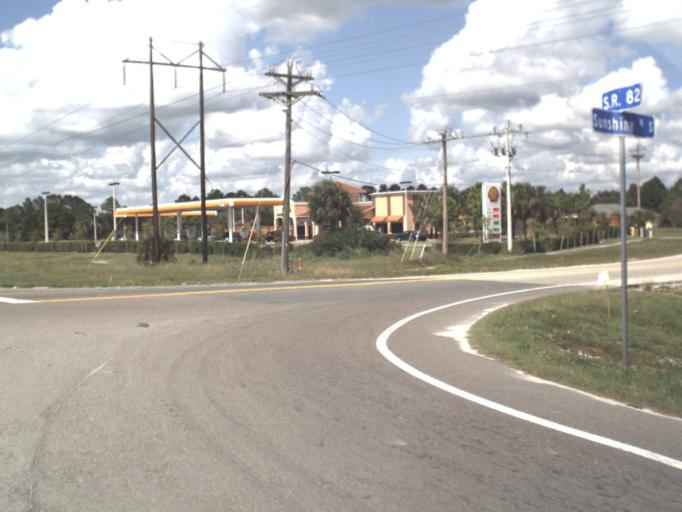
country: US
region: Florida
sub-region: Lee County
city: Gateway
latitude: 26.5663
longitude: -81.6781
